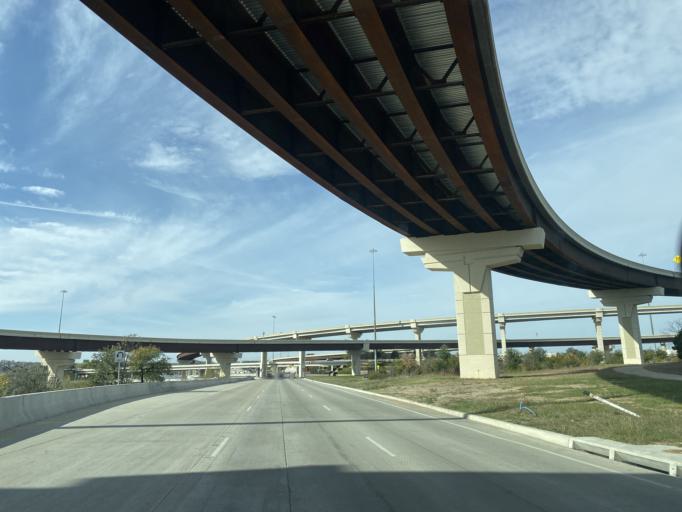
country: US
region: Texas
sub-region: Travis County
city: Austin
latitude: 30.3239
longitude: -97.6703
